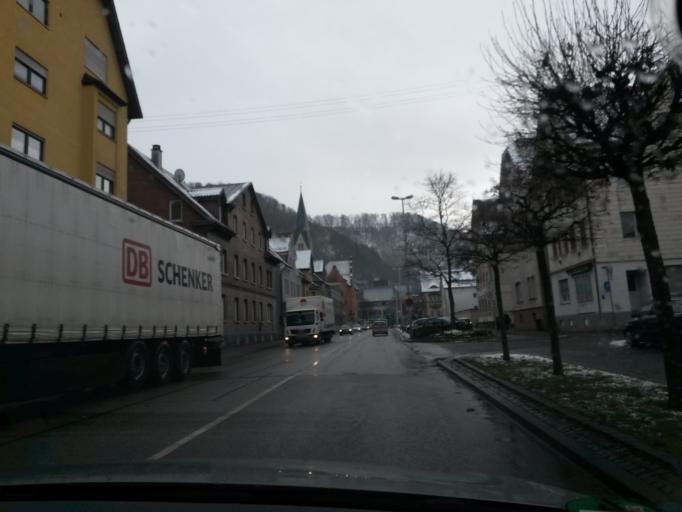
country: DE
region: Baden-Wuerttemberg
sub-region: Regierungsbezirk Stuttgart
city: Geislingen an der Steige
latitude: 48.6148
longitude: 9.8410
